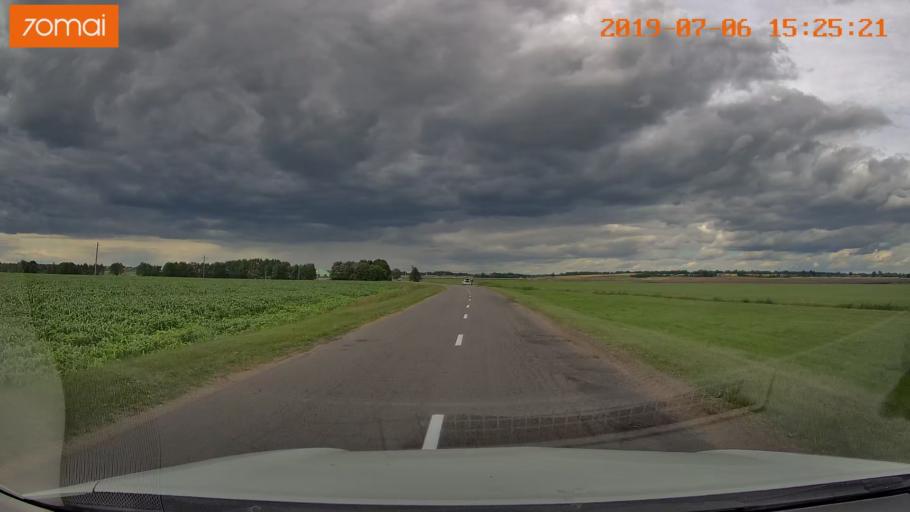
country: BY
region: Minsk
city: Valozhyn
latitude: 54.0307
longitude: 26.6042
